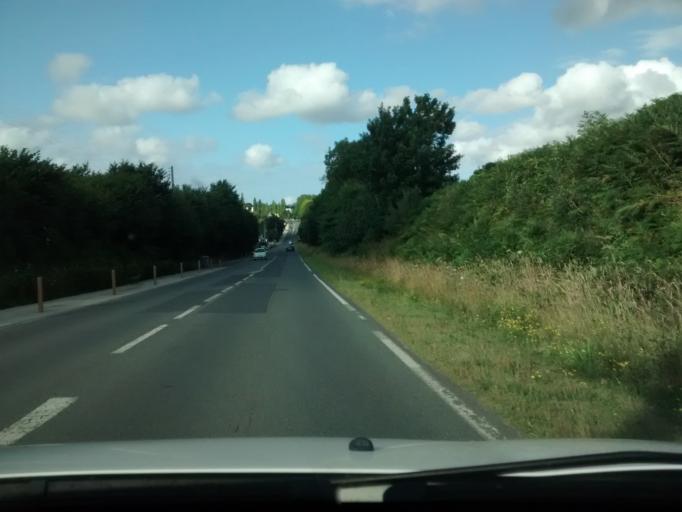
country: FR
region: Brittany
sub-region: Departement des Cotes-d'Armor
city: Lannion
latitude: 48.7366
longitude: -3.4347
